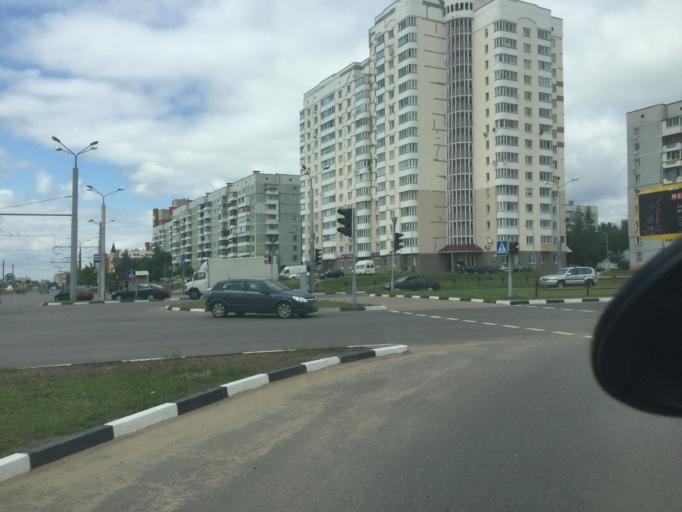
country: BY
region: Vitebsk
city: Vitebsk
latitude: 55.1619
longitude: 30.2220
